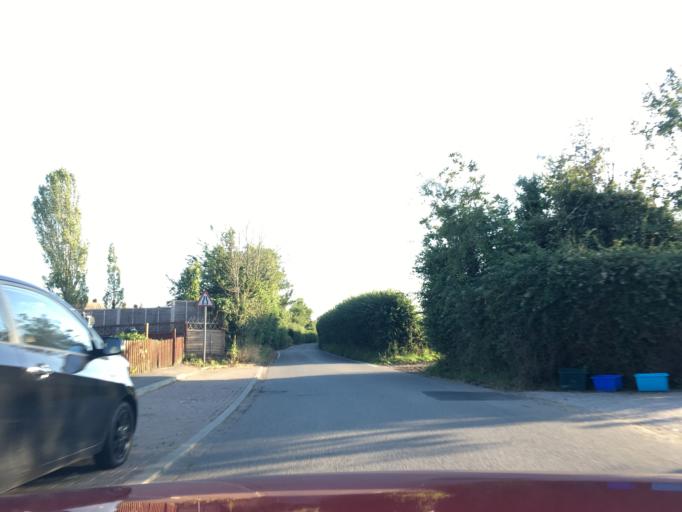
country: GB
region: England
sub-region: Hampshire
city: Tadley
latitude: 51.4171
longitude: -1.1503
